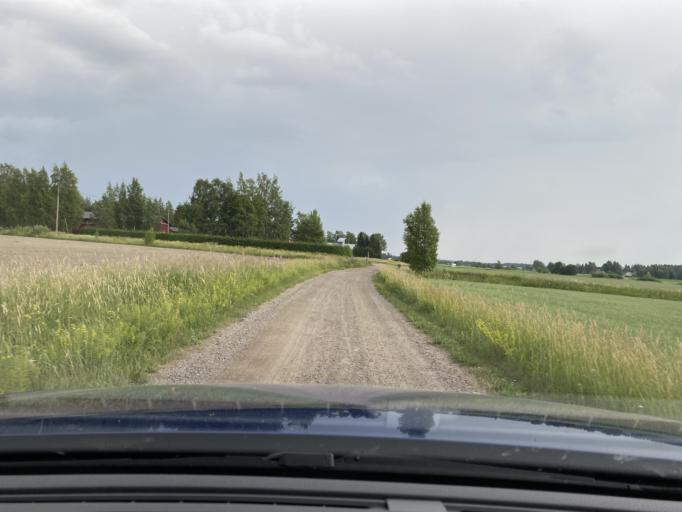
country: FI
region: Satakunta
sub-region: Rauma
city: Eura
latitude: 61.1576
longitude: 22.0954
